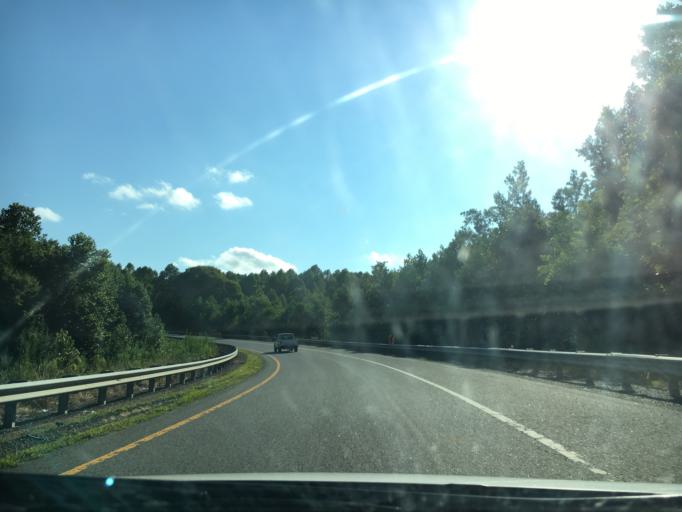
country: US
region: Virginia
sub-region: Amherst County
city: Madison Heights
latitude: 37.3891
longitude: -79.0926
